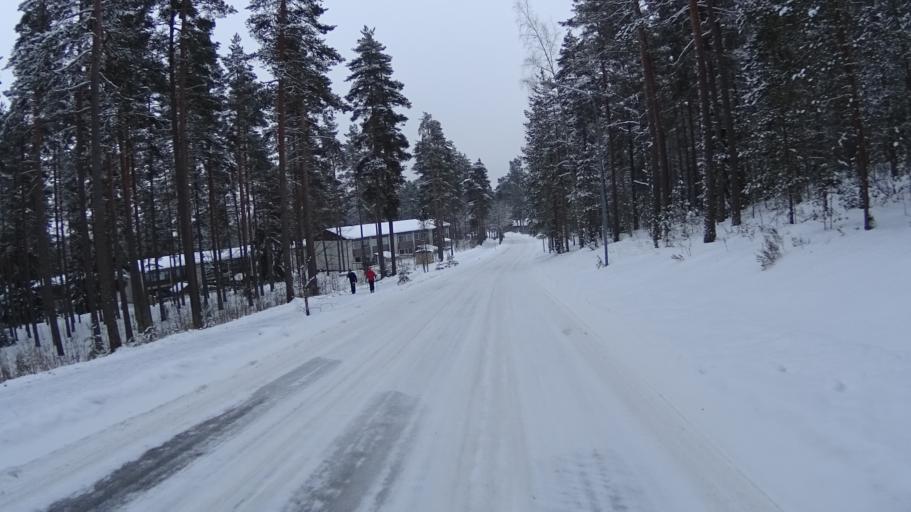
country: FI
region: Uusimaa
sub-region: Helsinki
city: Vihti
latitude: 60.3328
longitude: 24.2987
